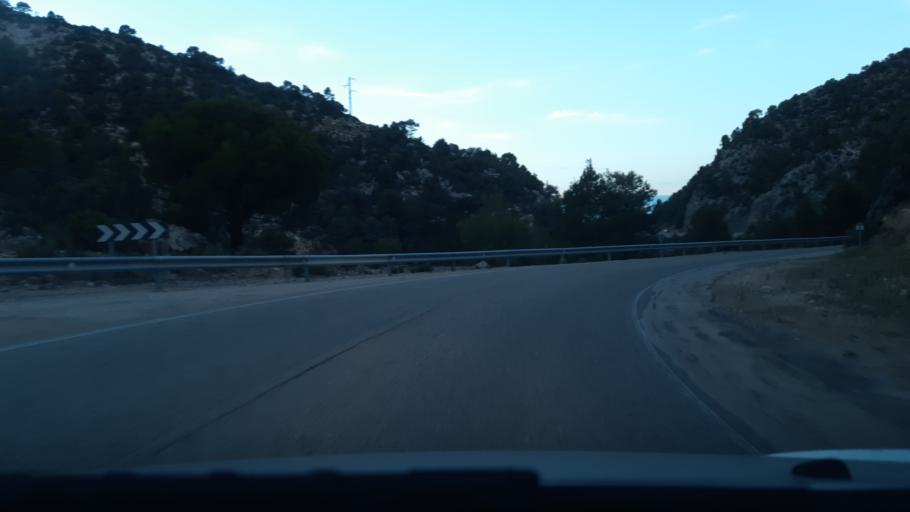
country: ES
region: Aragon
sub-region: Provincia de Teruel
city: Valderrobres
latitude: 40.8409
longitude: 0.1764
